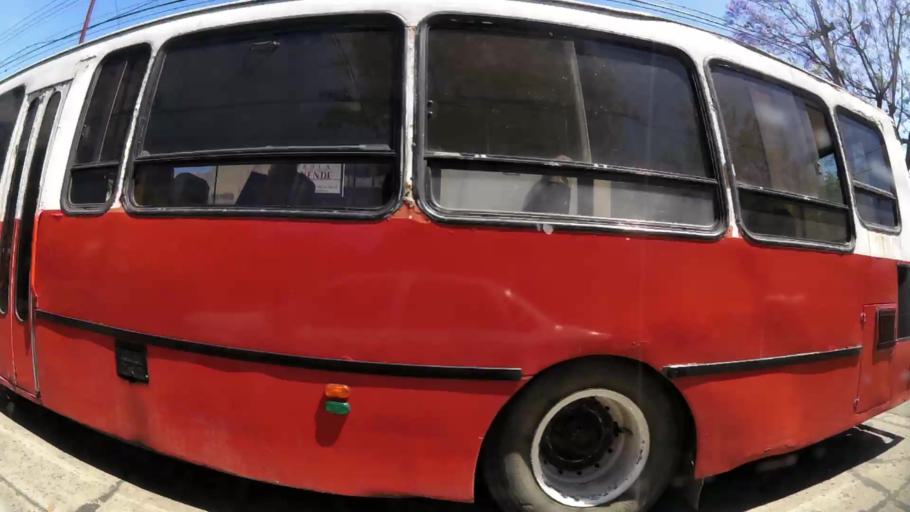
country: AR
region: Buenos Aires
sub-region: Partido de Merlo
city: Merlo
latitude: -34.6743
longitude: -58.6880
